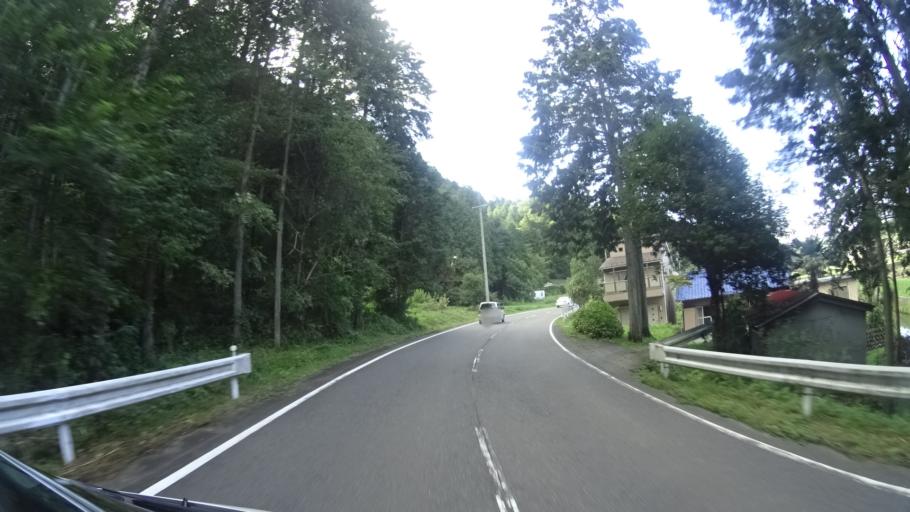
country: JP
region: Gifu
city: Minokamo
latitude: 35.5831
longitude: 137.0842
